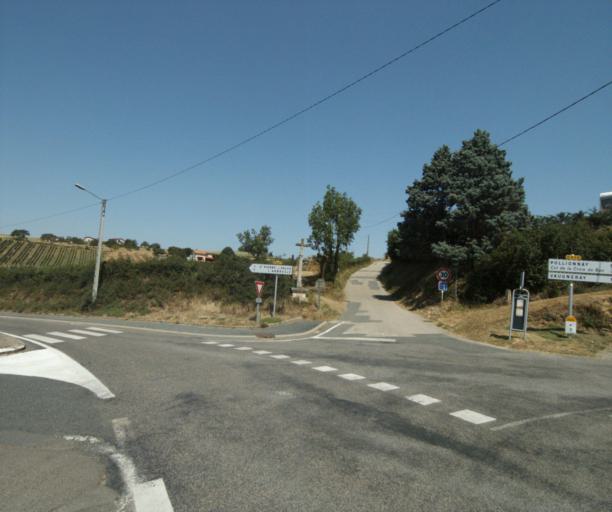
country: FR
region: Rhone-Alpes
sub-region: Departement du Rhone
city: Saint-Pierre-la-Palud
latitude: 45.7848
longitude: 4.6192
